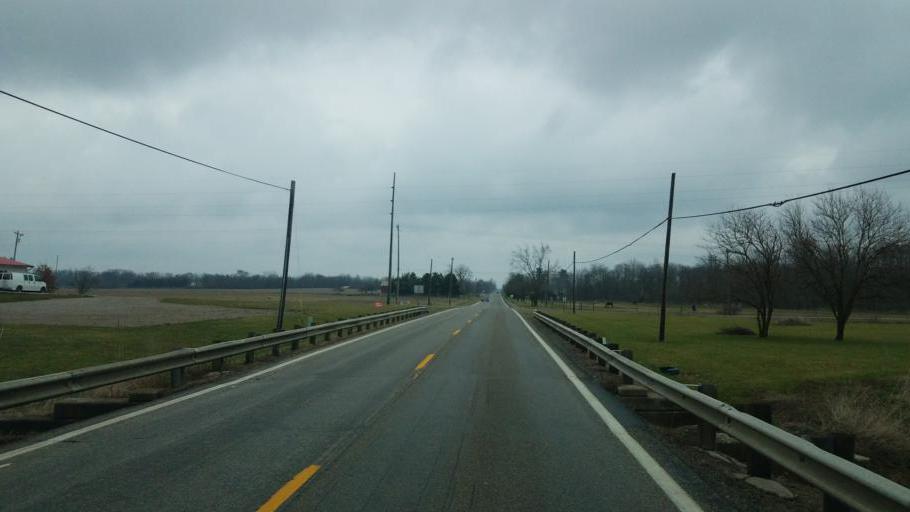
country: US
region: Ohio
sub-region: Delaware County
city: Ashley
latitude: 40.4073
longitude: -82.9121
